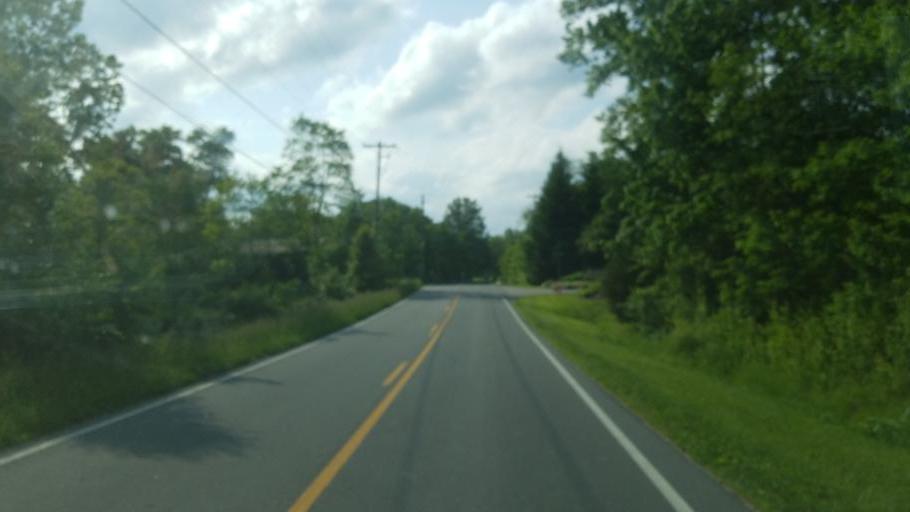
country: US
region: Ohio
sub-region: Delaware County
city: Sunbury
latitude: 40.1834
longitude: -82.8689
